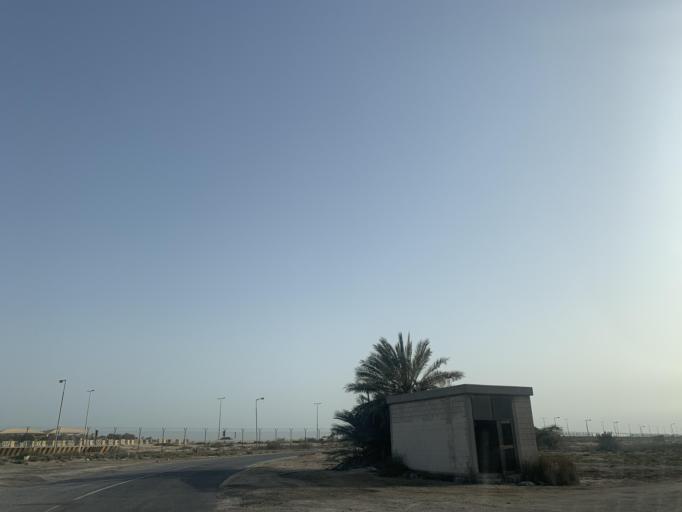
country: BH
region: Central Governorate
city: Madinat Hamad
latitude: 26.1729
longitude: 50.4516
